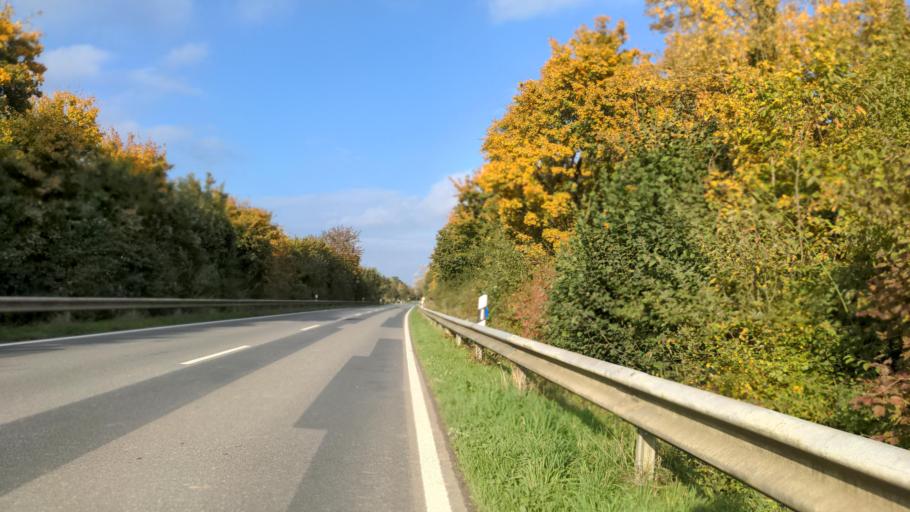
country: DE
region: Schleswig-Holstein
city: Beschendorf
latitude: 54.1749
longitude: 10.8751
